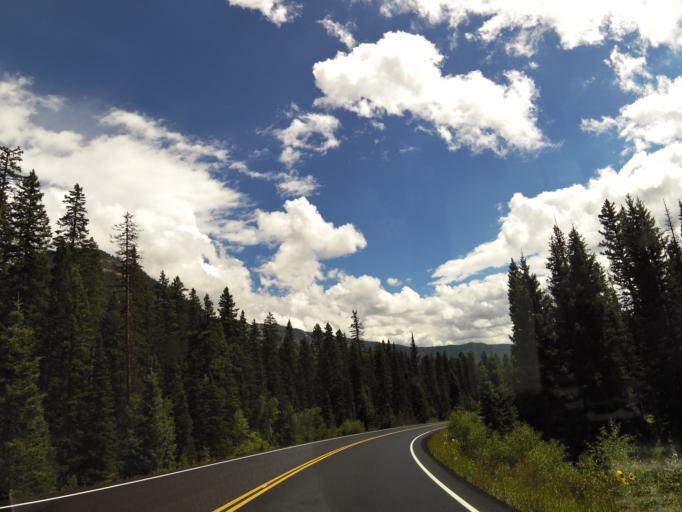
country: US
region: Colorado
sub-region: San Juan County
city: Silverton
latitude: 37.6763
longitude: -107.7915
